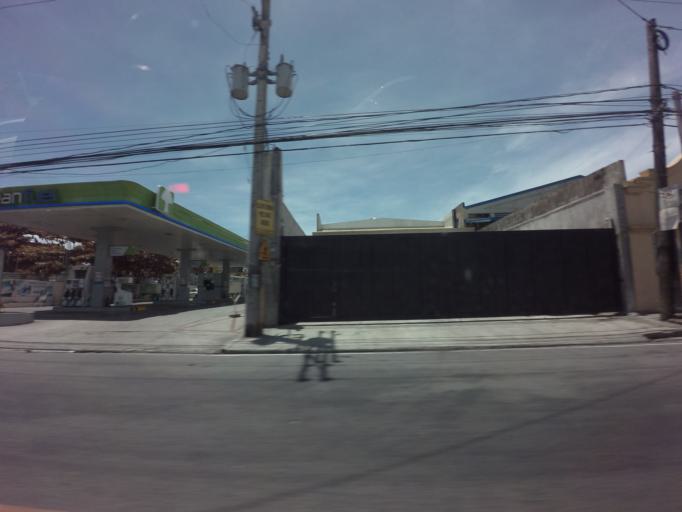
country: PH
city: Sambayanihan People's Village
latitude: 14.4903
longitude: 120.9919
